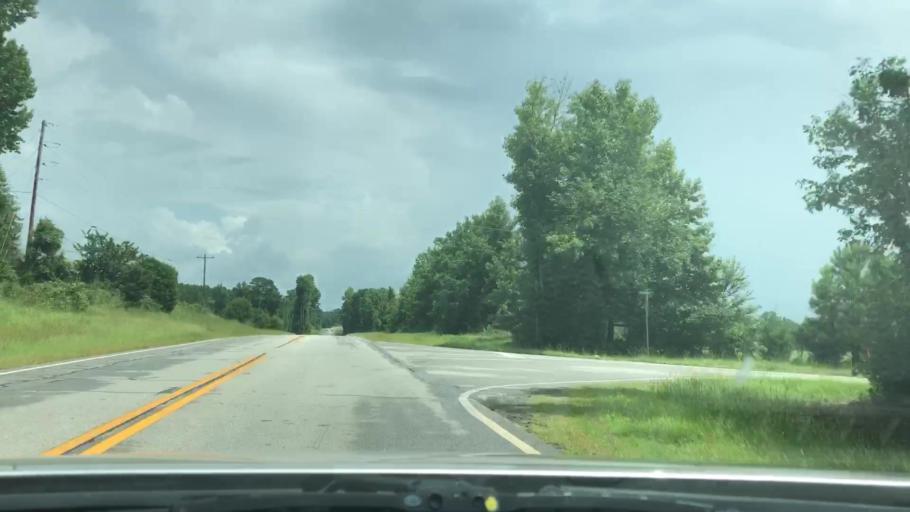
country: US
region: Georgia
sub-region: Pike County
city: Zebulon
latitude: 33.1033
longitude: -84.3233
